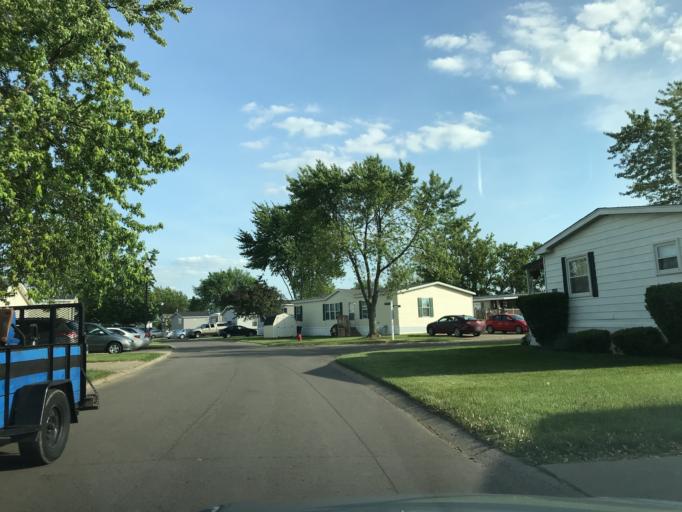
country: US
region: Michigan
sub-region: Oakland County
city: Walled Lake
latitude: 42.5148
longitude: -83.4601
